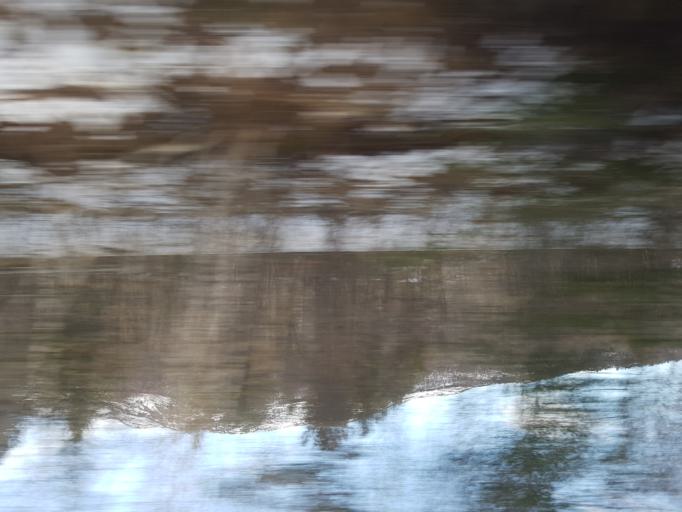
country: NO
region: Sor-Trondelag
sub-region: Oppdal
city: Oppdal
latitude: 62.6146
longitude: 9.7511
